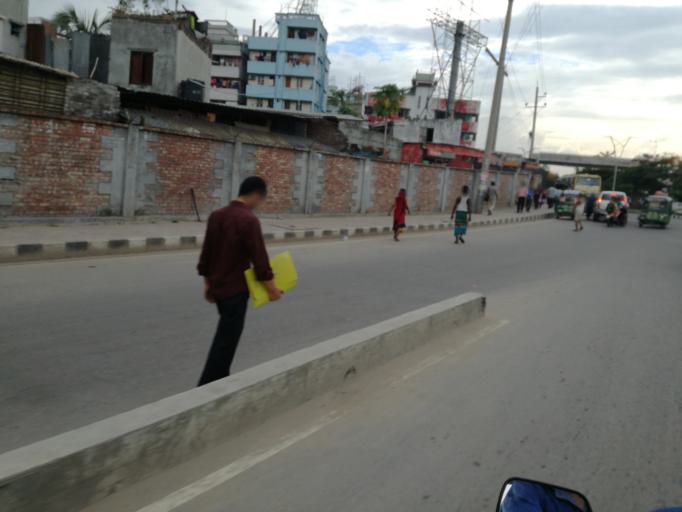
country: BD
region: Dhaka
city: Paltan
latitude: 23.7678
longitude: 90.4226
